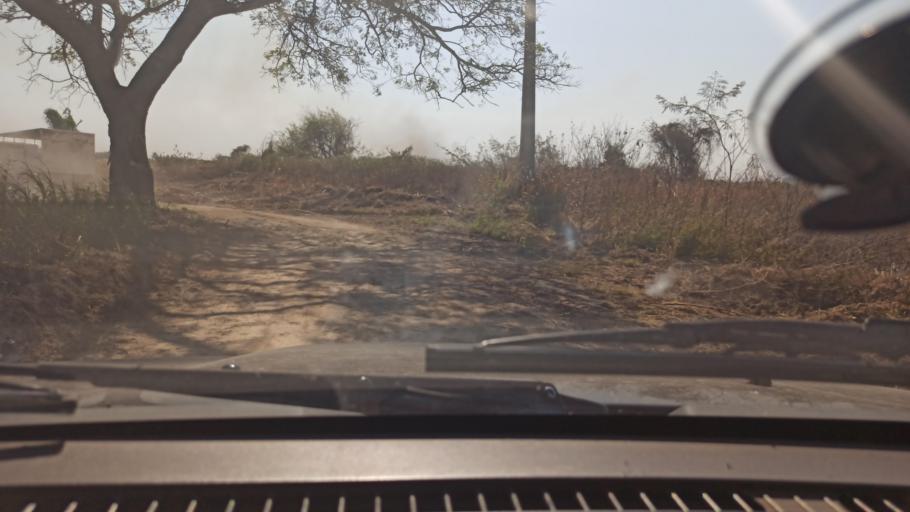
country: PY
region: Asuncion
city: Asuncion
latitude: -25.3431
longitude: -57.6757
